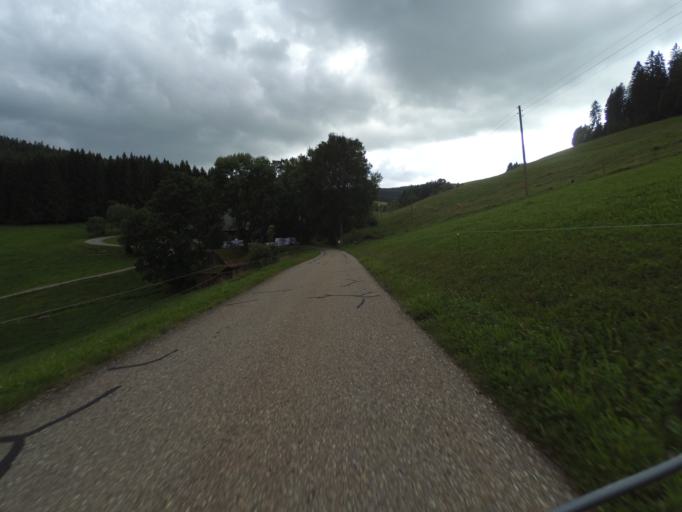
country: DE
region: Baden-Wuerttemberg
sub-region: Freiburg Region
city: Titisee-Neustadt
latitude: 47.9522
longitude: 8.1427
